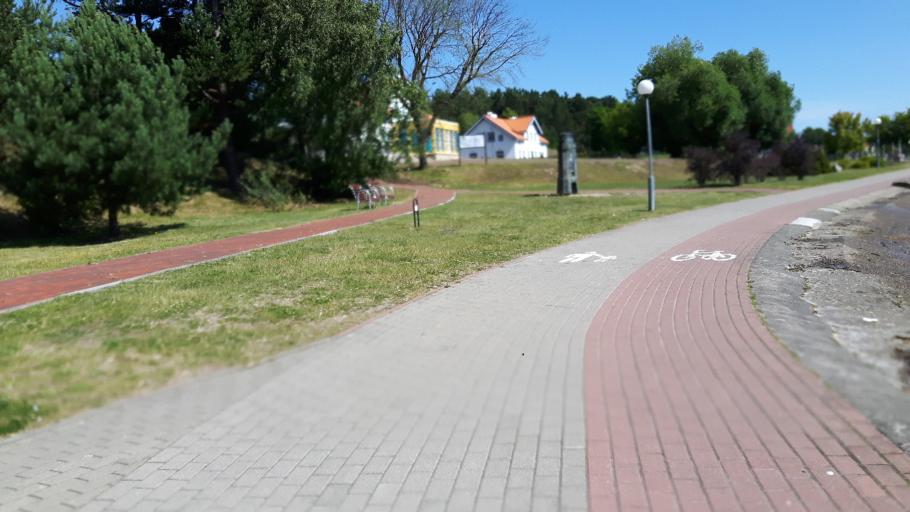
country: LT
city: Nida
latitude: 55.3141
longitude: 21.0151
